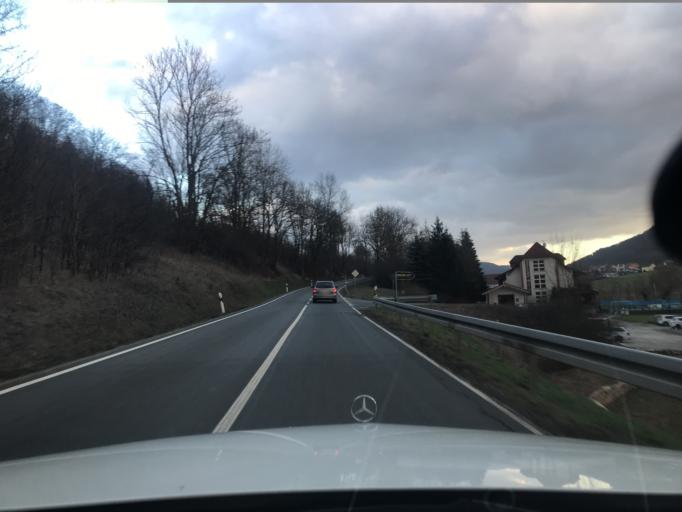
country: DE
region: Thuringia
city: Grossbartloff
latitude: 51.2190
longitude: 10.2050
